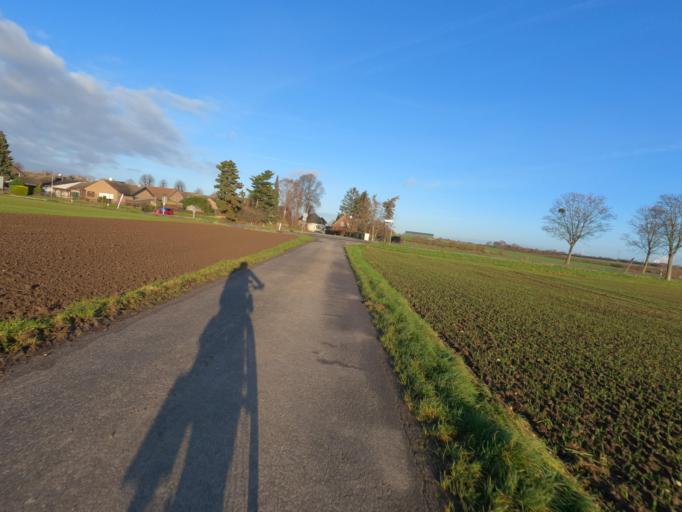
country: DE
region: North Rhine-Westphalia
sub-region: Regierungsbezirk Koln
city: Elsdorf
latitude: 50.9651
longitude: 6.5512
